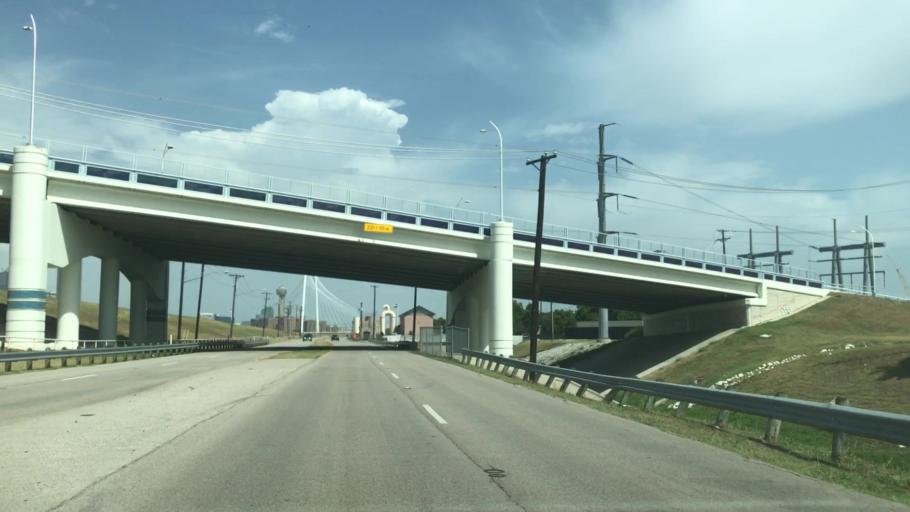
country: US
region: Texas
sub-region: Dallas County
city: Dallas
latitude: 32.7862
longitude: -96.8365
